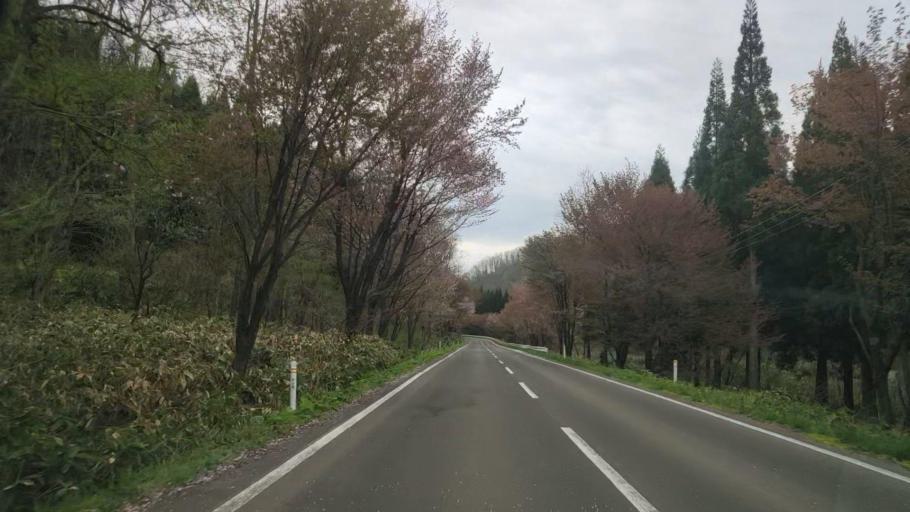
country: JP
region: Akita
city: Hanawa
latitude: 40.3515
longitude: 140.7766
